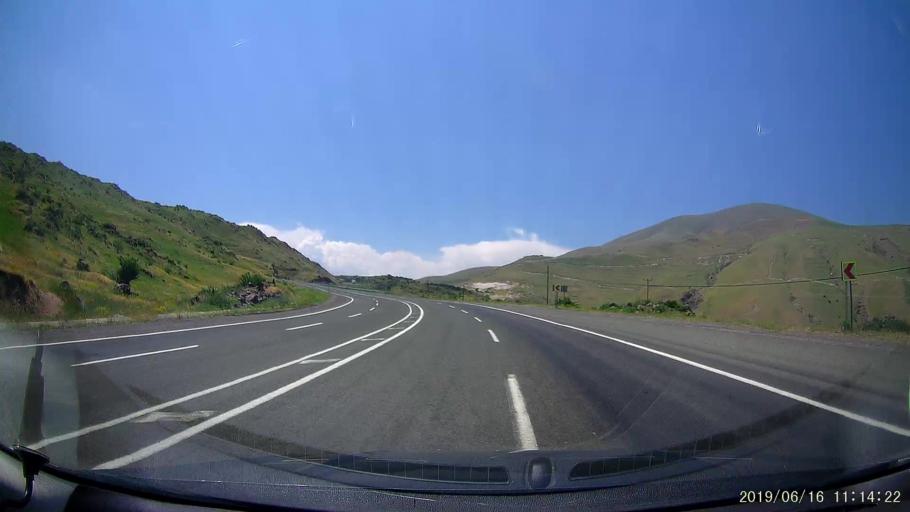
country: TR
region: Igdir
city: Igdir
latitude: 39.7803
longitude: 44.1426
